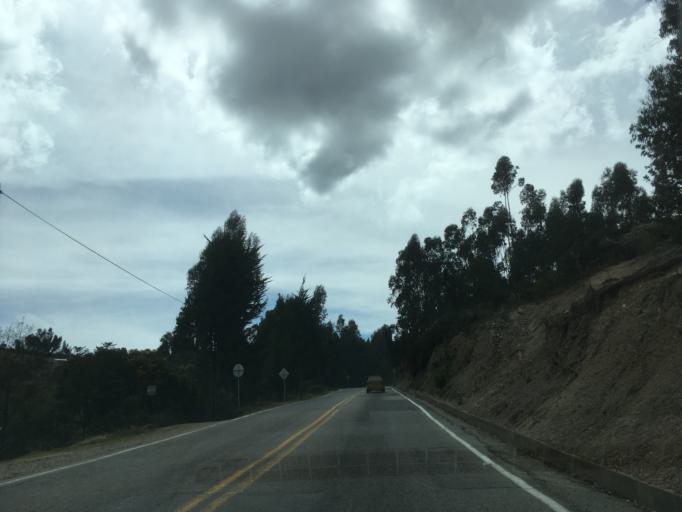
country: CO
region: Boyaca
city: Sogamoso
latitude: 5.6415
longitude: -72.9210
